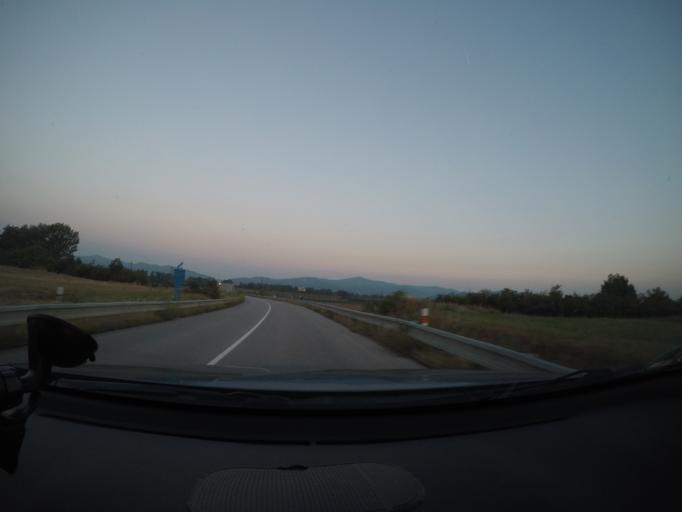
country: SK
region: Trenciansky
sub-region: Okres Trencin
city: Trencin
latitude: 48.8756
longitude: 17.9670
